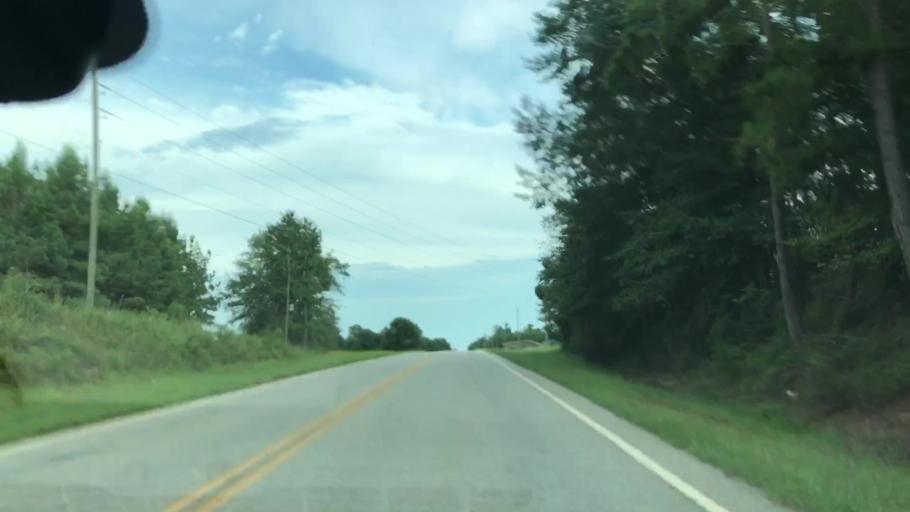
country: US
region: Georgia
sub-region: Quitman County
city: Georgetown
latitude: 31.7637
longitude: -85.0817
